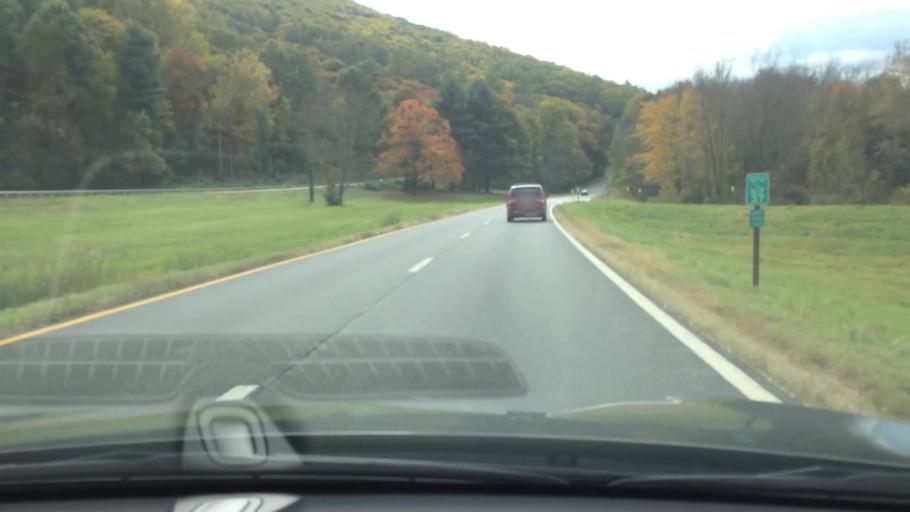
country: US
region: New York
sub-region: Dutchess County
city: Hillside Lake
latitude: 41.5360
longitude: -73.7718
